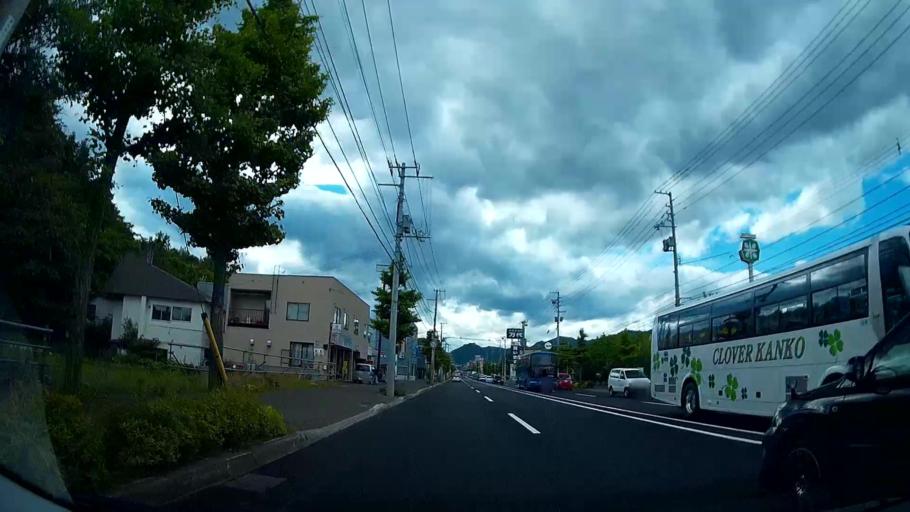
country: JP
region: Hokkaido
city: Sapporo
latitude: 42.9611
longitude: 141.3073
